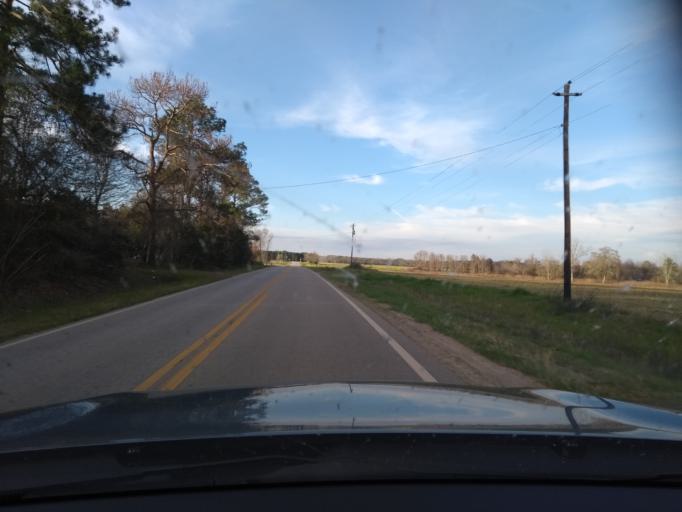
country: US
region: Georgia
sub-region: Bulloch County
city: Statesboro
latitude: 32.3247
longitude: -81.7753
